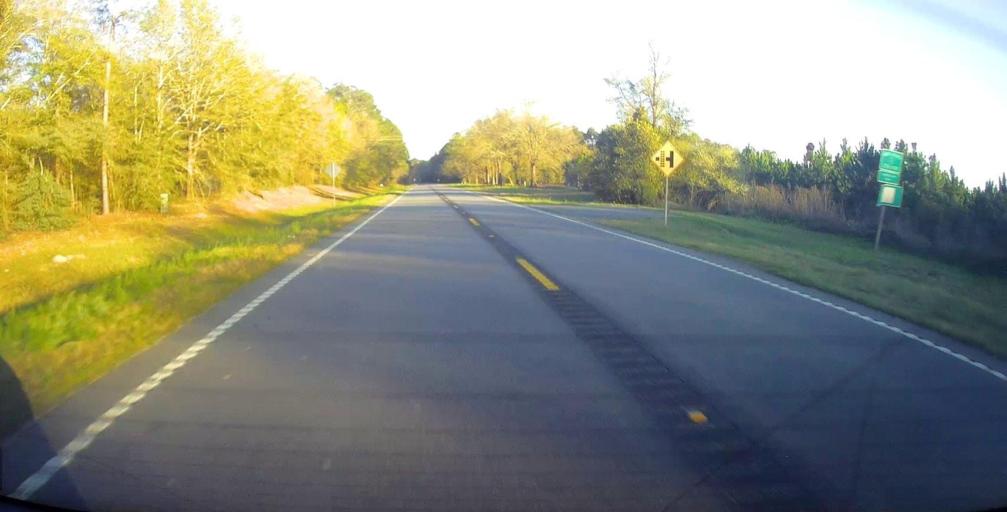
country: US
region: Georgia
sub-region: Wilcox County
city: Rochelle
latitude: 31.9553
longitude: -83.5791
